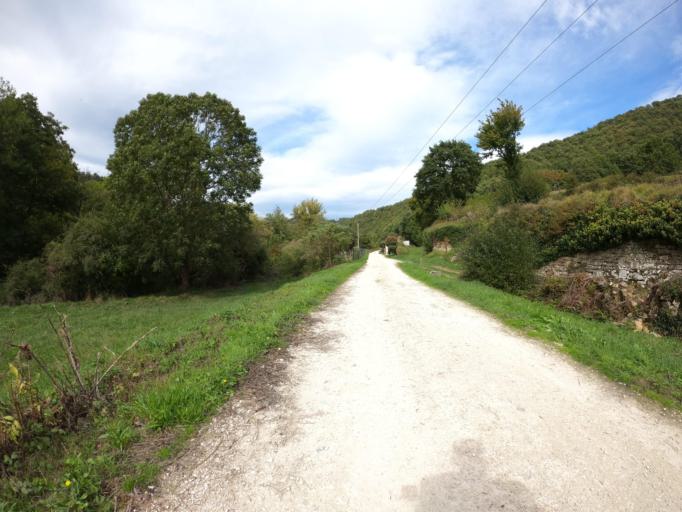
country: ES
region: Navarre
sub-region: Provincia de Navarra
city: Irurtzun
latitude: 42.9573
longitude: -1.8241
